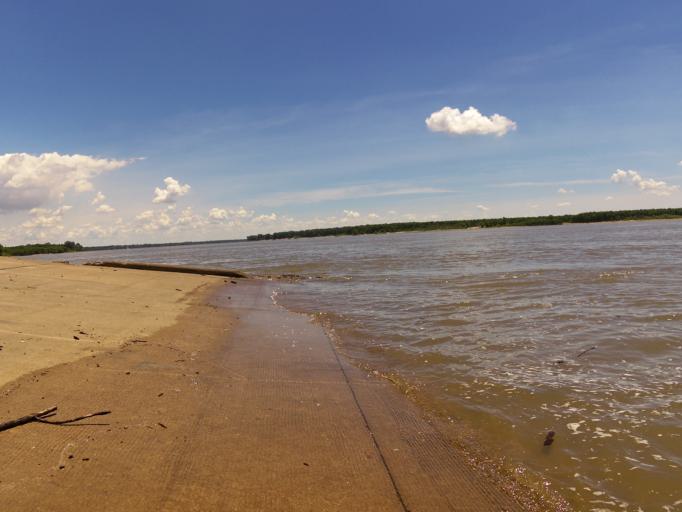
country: US
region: Missouri
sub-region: New Madrid County
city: New Madrid
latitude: 36.5828
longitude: -89.5335
